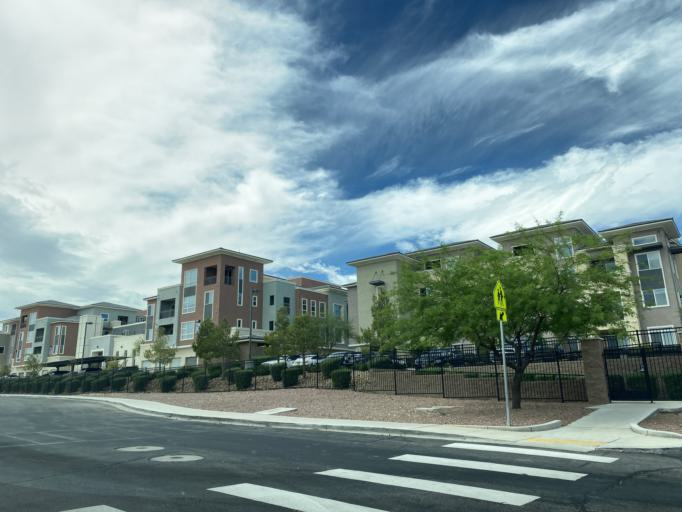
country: US
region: Nevada
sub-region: Clark County
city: Whitney
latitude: 36.0239
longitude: -115.0795
